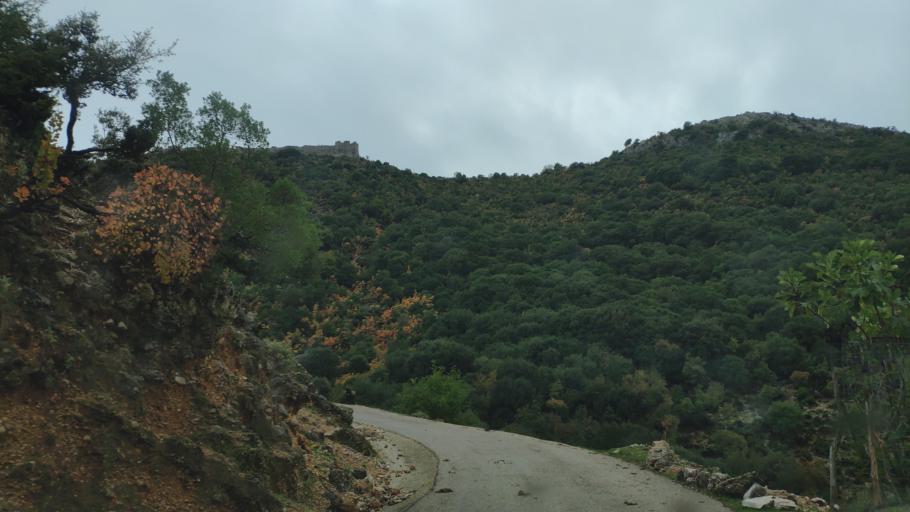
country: GR
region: Epirus
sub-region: Nomos Prevezis
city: Kanalaki
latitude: 39.3401
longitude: 20.6527
